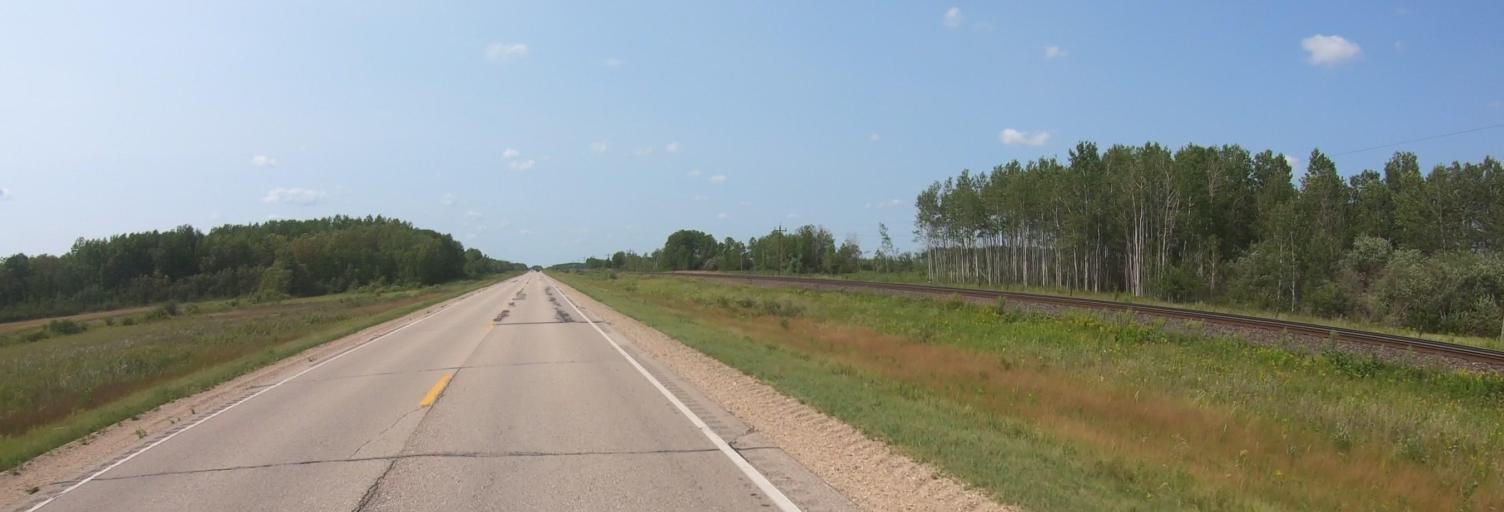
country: US
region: Minnesota
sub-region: Lake of the Woods County
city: Baudette
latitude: 48.7313
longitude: -94.7988
